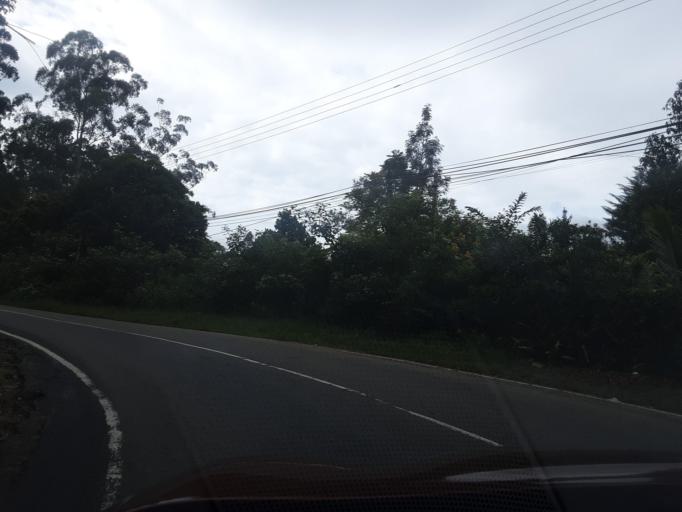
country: LK
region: Uva
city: Haputale
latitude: 6.8532
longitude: 80.9684
